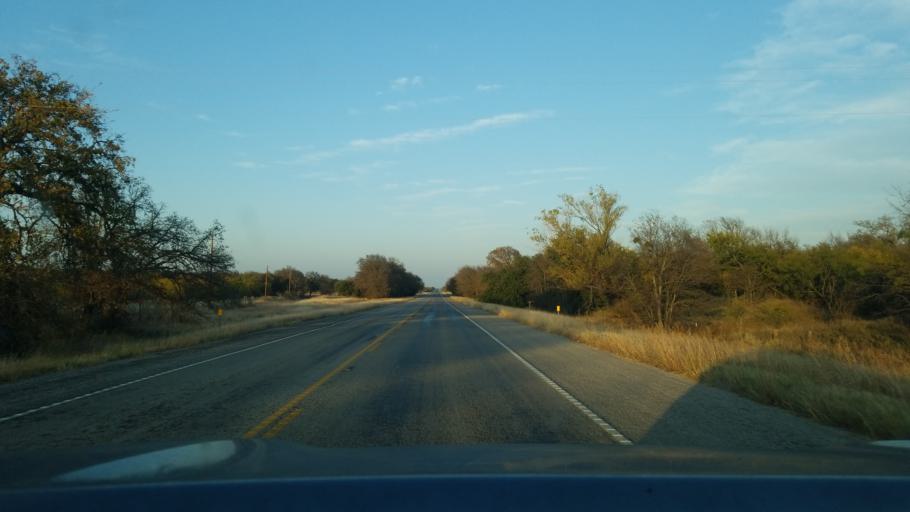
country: US
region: Texas
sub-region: Eastland County
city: Cisco
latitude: 32.4124
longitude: -98.9451
